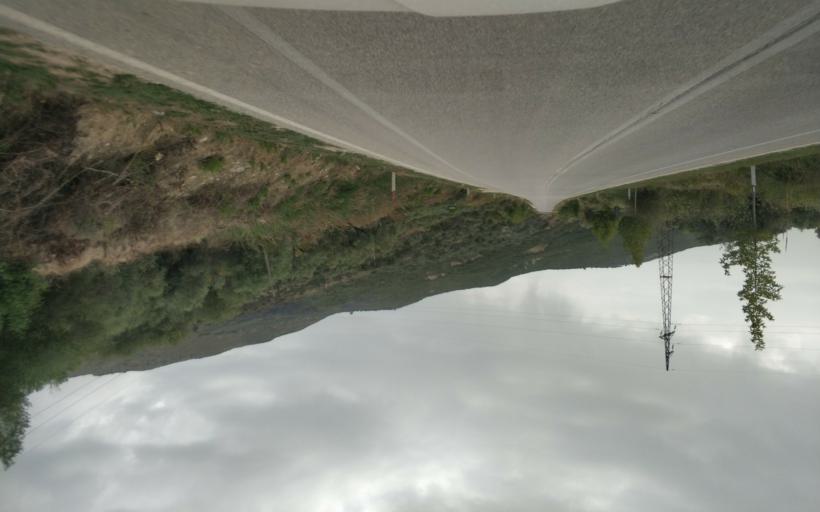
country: AL
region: Fier
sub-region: Rrethi i Mallakastres
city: Hekal
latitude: 40.5202
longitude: 19.7415
